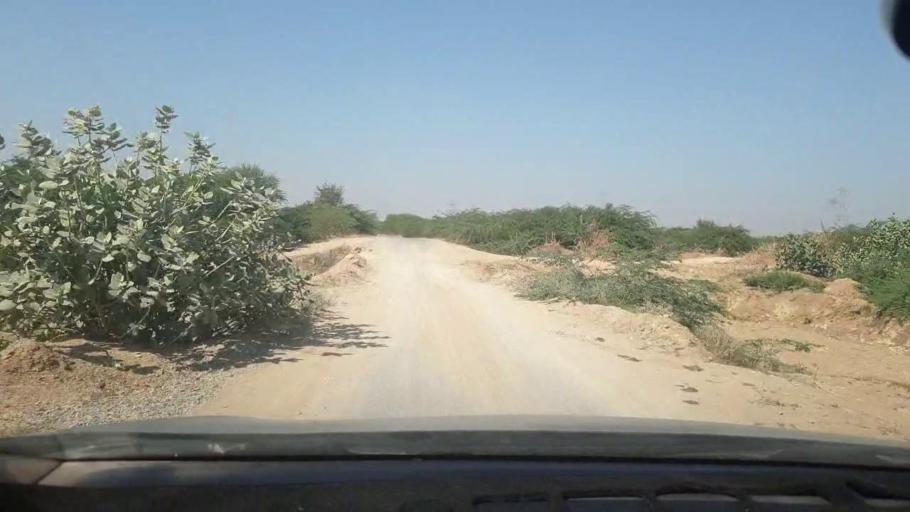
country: PK
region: Sindh
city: Malir Cantonment
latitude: 25.1612
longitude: 67.1615
